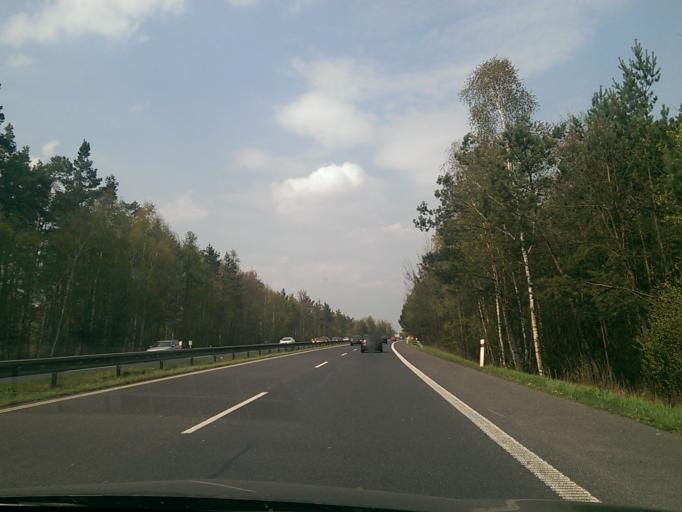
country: CZ
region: Central Bohemia
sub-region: Okres Mlada Boleslav
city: Mlada Boleslav
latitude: 50.3520
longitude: 14.8717
